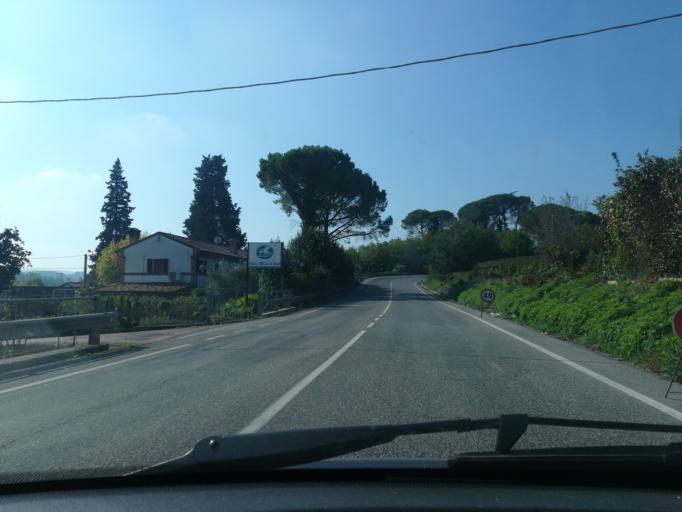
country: IT
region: The Marches
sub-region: Provincia di Macerata
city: Piediripa
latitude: 43.2701
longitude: 13.4700
